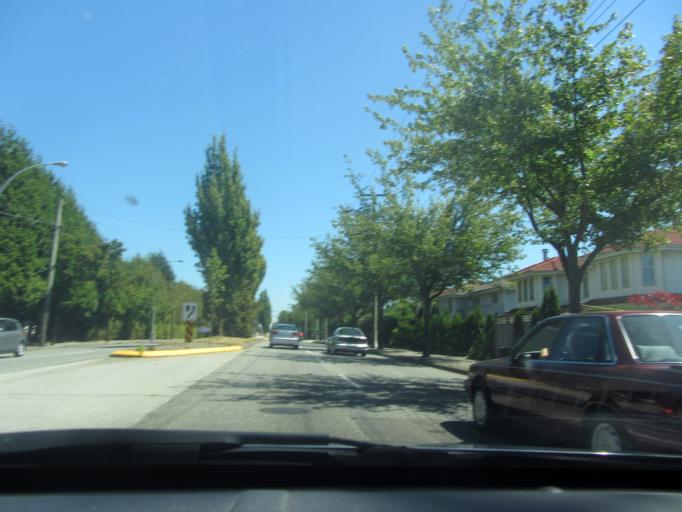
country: CA
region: British Columbia
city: Delta
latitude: 49.1339
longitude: -122.8836
